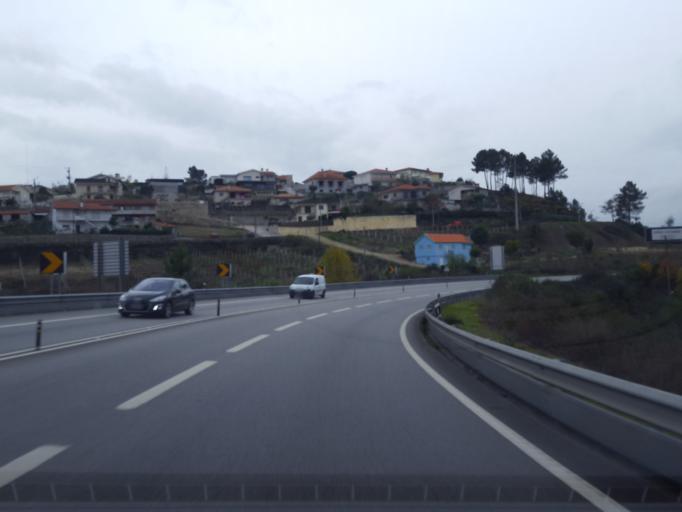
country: PT
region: Porto
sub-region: Marco de Canaveses
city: Marco de Canavezes
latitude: 41.2119
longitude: -8.1677
